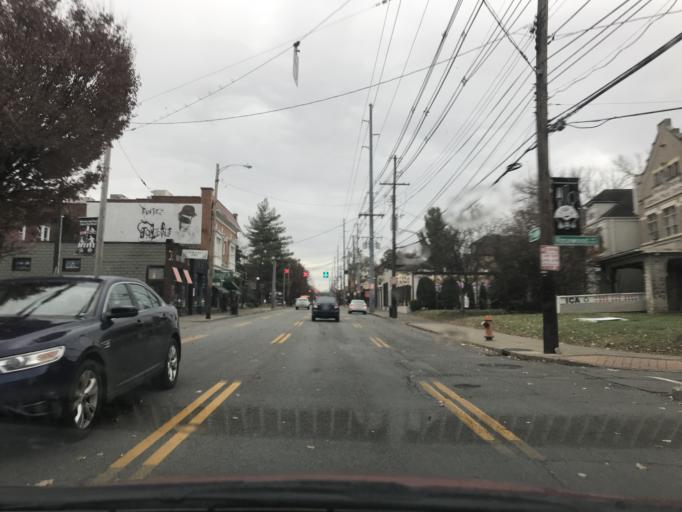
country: US
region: Kentucky
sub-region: Jefferson County
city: Audubon Park
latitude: 38.2353
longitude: -85.7154
